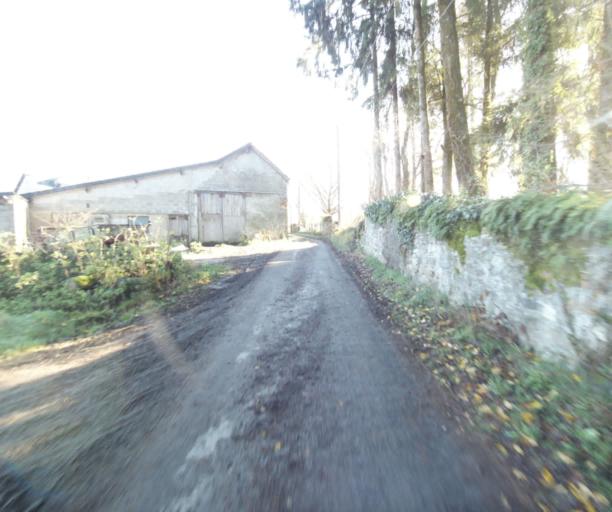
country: FR
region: Limousin
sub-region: Departement de la Correze
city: Laguenne
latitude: 45.2377
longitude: 1.7491
